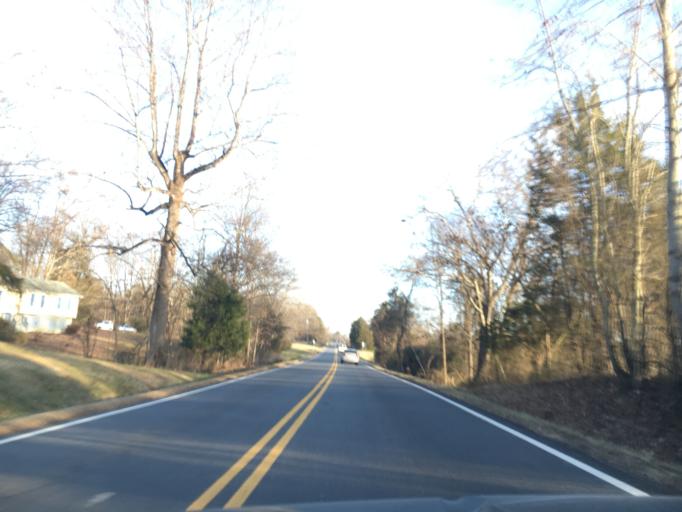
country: US
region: Virginia
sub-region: Culpeper County
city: Merrimac
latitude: 38.5151
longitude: -78.0735
